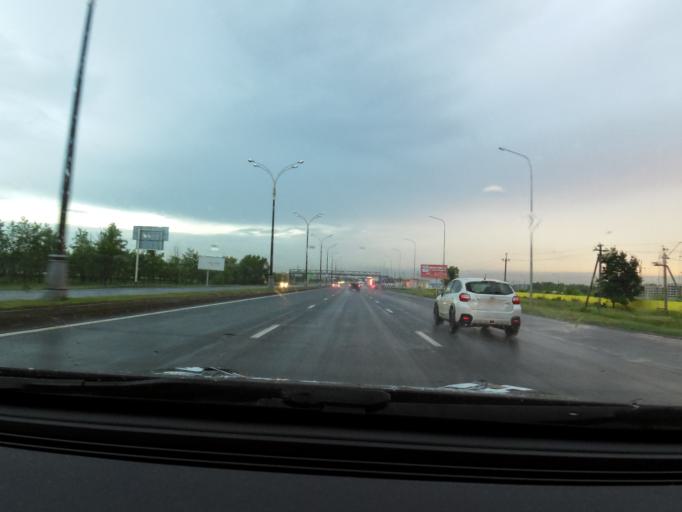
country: RU
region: Tatarstan
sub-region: Tukayevskiy Rayon
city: Naberezhnyye Chelny
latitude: 55.6738
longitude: 52.3281
